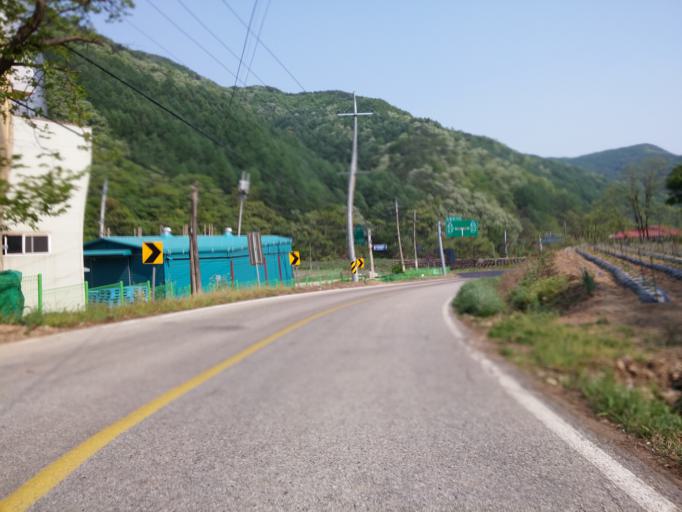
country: KR
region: Chungcheongbuk-do
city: Okcheon
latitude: 36.4116
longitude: 127.6406
